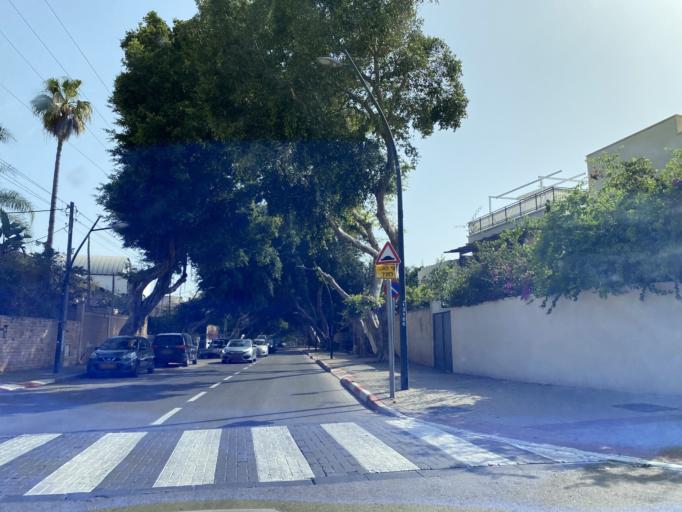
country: IL
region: Tel Aviv
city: Herzliya Pituah
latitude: 32.1725
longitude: 34.8077
